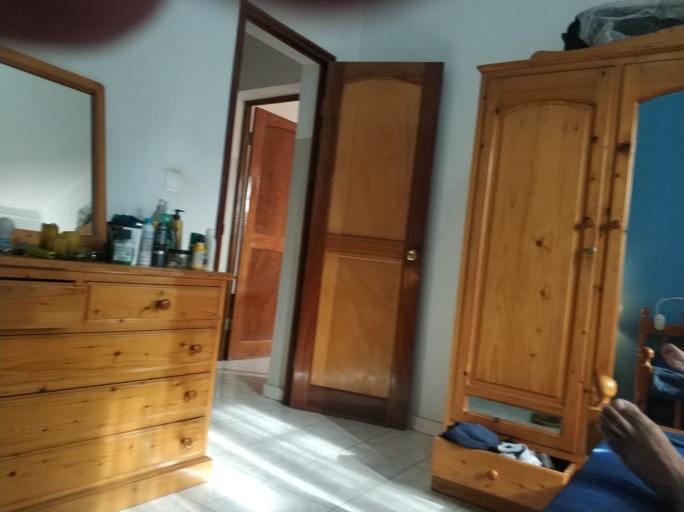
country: CV
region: Sao Filipe
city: Sao Filipe
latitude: 14.8983
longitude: -24.4981
